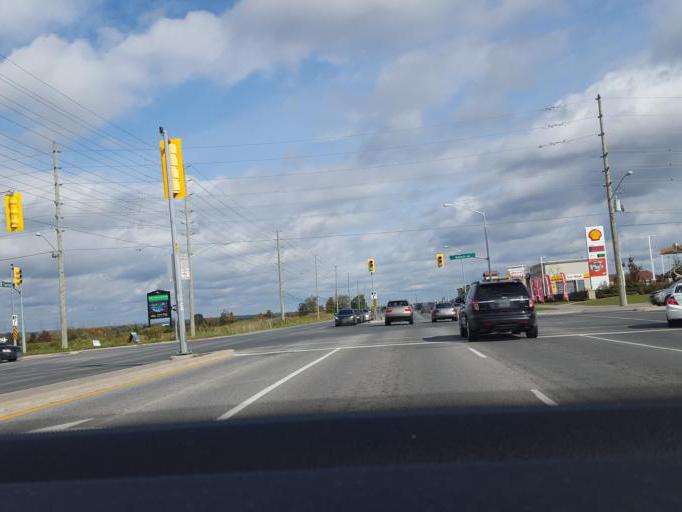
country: CA
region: Ontario
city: Ajax
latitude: 43.8979
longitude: -79.0313
